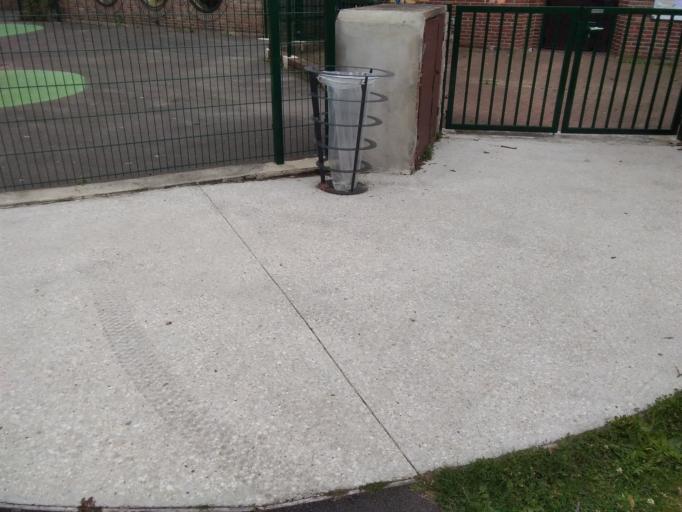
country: FR
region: Picardie
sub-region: Departement de la Somme
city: Amiens
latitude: 49.9221
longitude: 2.2974
